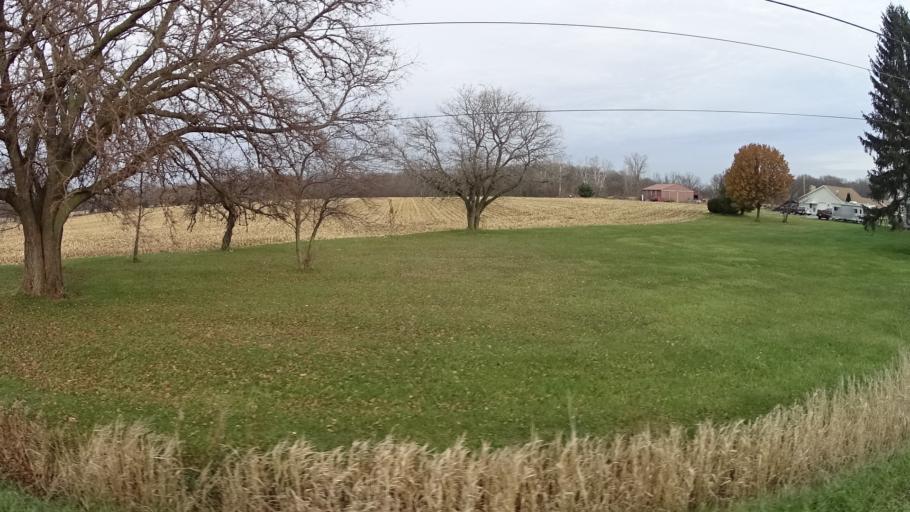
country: US
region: Ohio
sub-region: Lorain County
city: Lagrange
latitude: 41.1366
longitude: -82.1022
